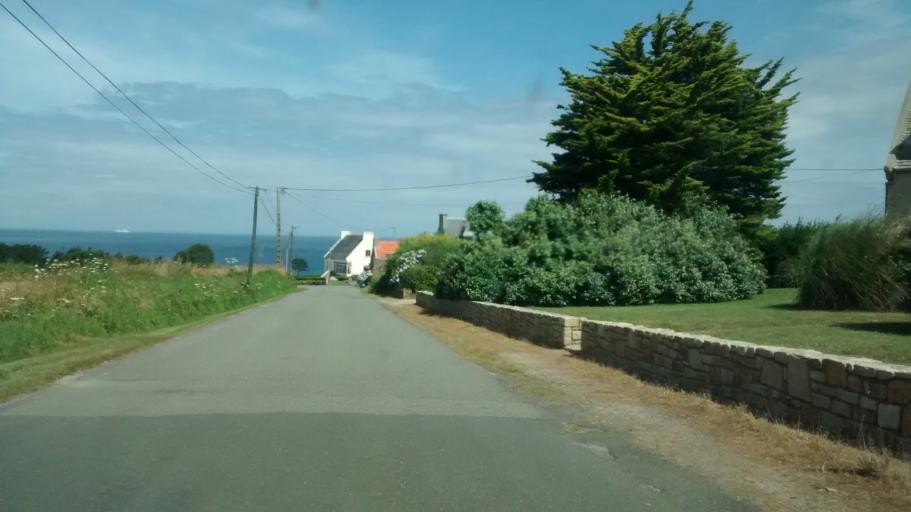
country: FR
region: Brittany
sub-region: Departement du Finistere
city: Plouguerneau
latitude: 48.6197
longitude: -4.4795
